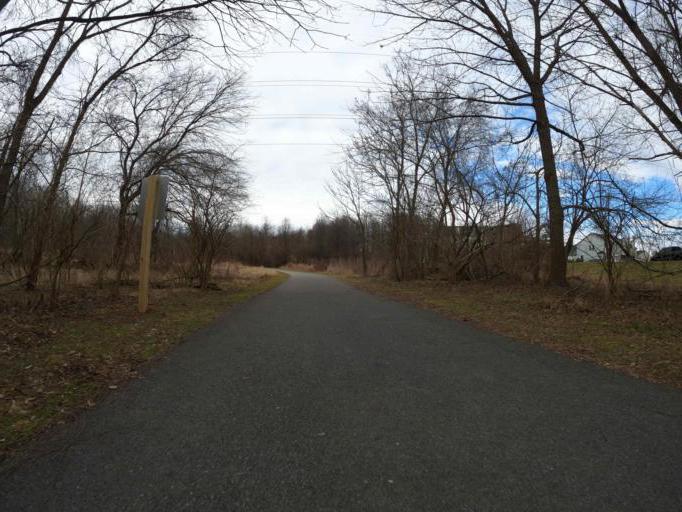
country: US
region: Maryland
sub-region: Frederick County
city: Ballenger Creek
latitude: 39.3739
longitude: -77.4270
